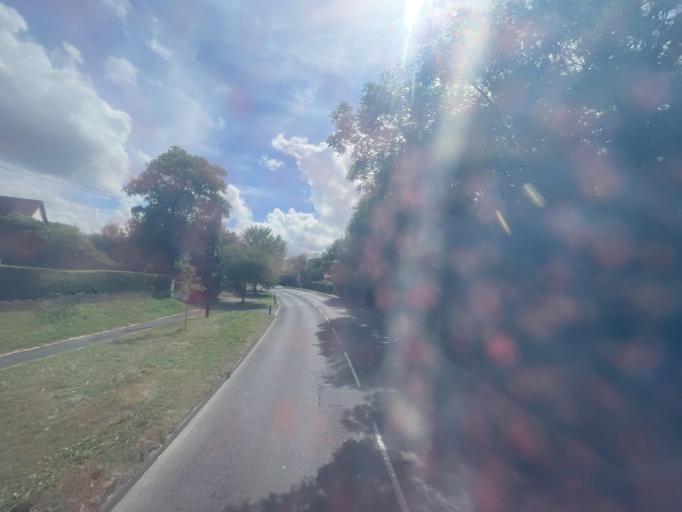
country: GB
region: England
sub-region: Kent
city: Biggin Hill
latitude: 51.3425
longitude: 0.0310
